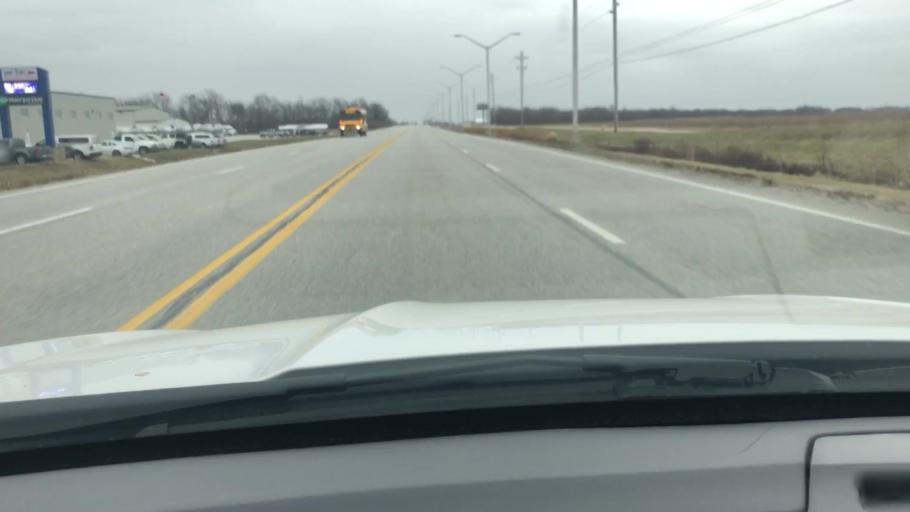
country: US
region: Indiana
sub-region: Tippecanoe County
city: Lafayette
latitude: 40.3673
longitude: -86.8551
